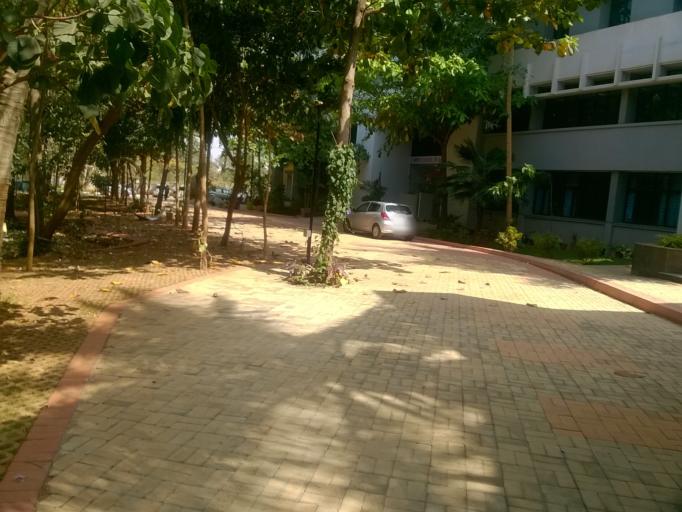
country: IN
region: Karnataka
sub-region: Bangalore Urban
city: Yelahanka
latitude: 13.1326
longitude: 77.5680
